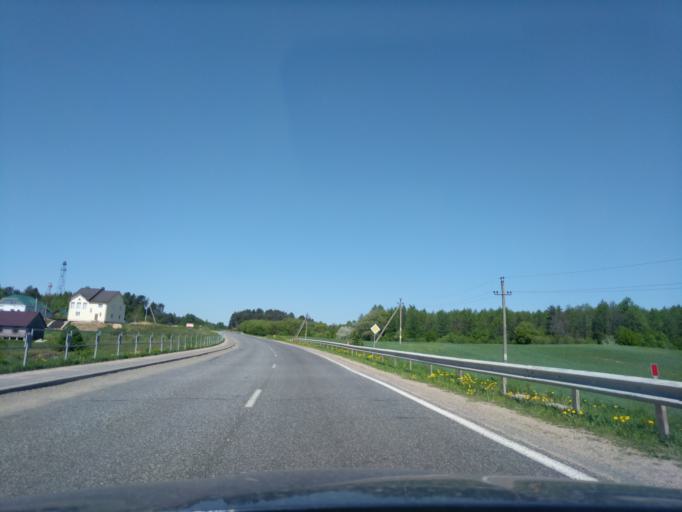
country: BY
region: Minsk
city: Myadzyel
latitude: 54.8923
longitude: 26.9115
